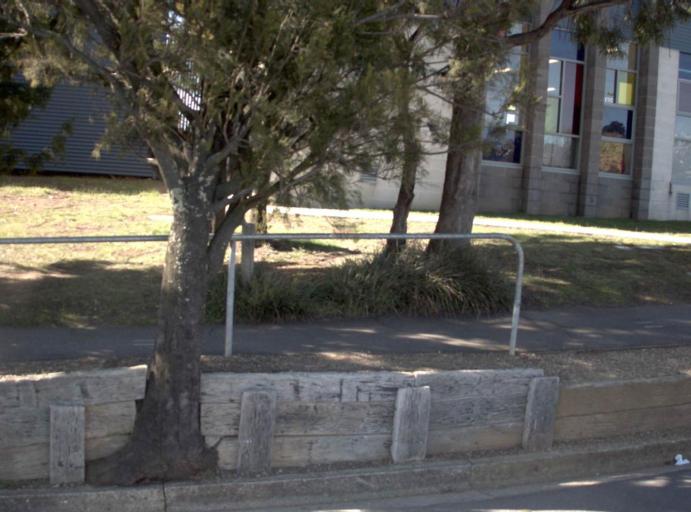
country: AU
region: Tasmania
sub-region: Launceston
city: Newstead
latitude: -41.4519
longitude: 147.1642
